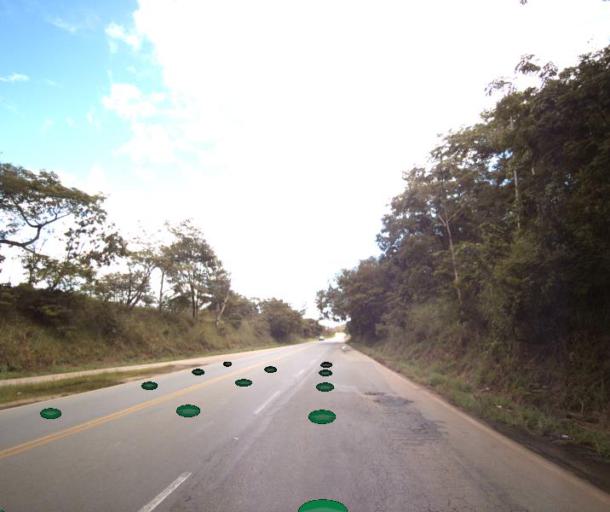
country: BR
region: Goias
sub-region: Jaragua
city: Jaragua
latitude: -15.8940
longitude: -49.2386
